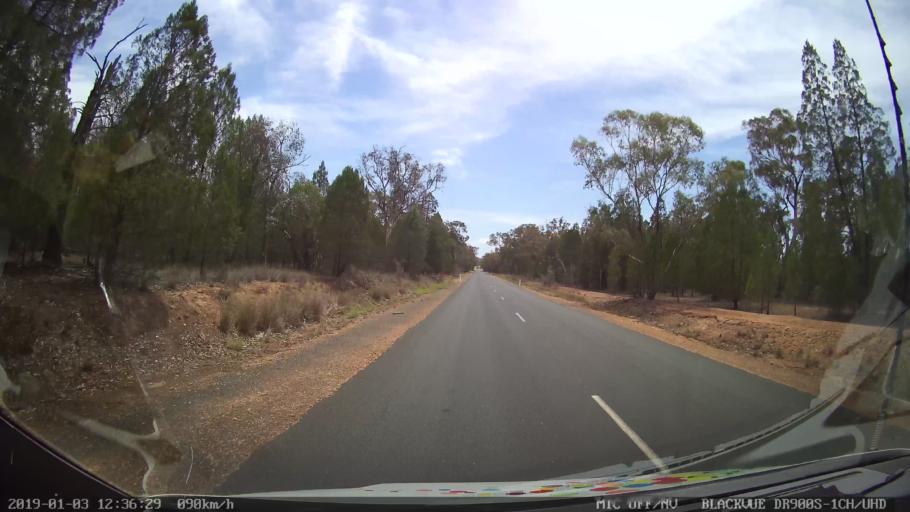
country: AU
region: New South Wales
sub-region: Weddin
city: Grenfell
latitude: -33.8544
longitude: 148.1771
